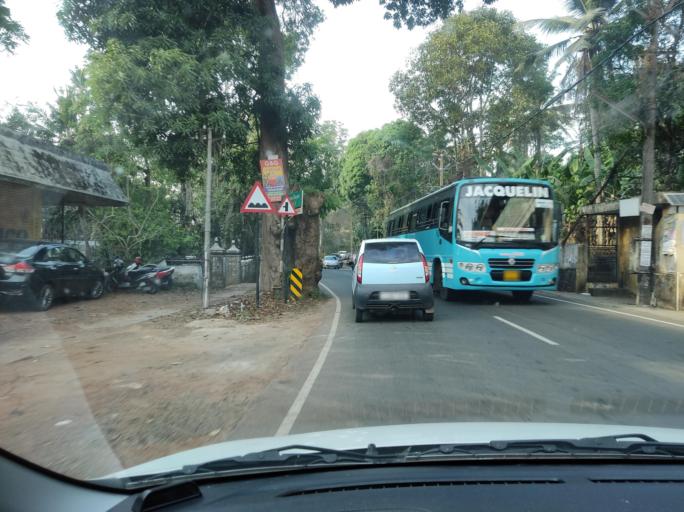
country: IN
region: Kerala
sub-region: Kottayam
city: Kottayam
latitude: 9.6434
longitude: 76.5339
